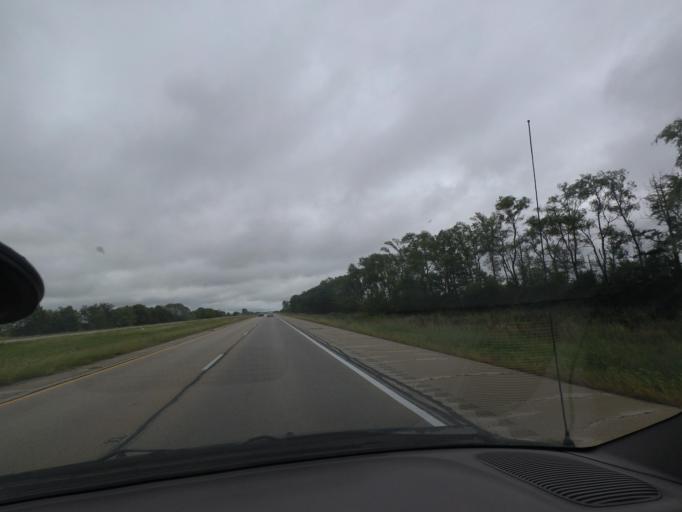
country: US
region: Illinois
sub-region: Piatt County
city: Cerro Gordo
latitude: 40.0198
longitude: -88.7113
